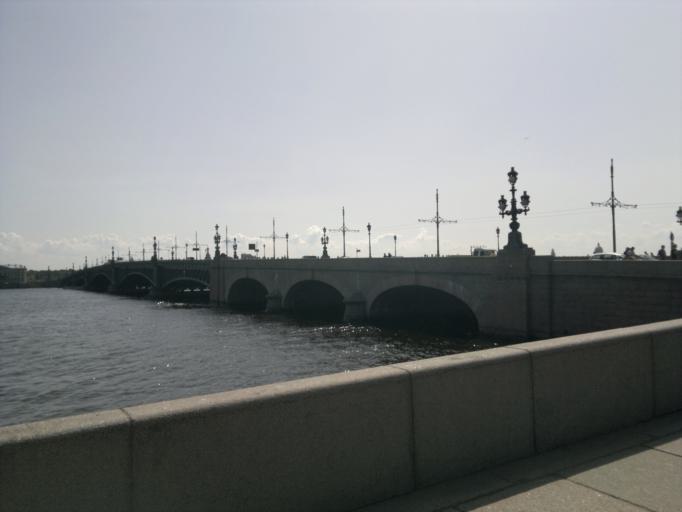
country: RU
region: St.-Petersburg
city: Saint Petersburg
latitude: 59.9514
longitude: 30.3261
